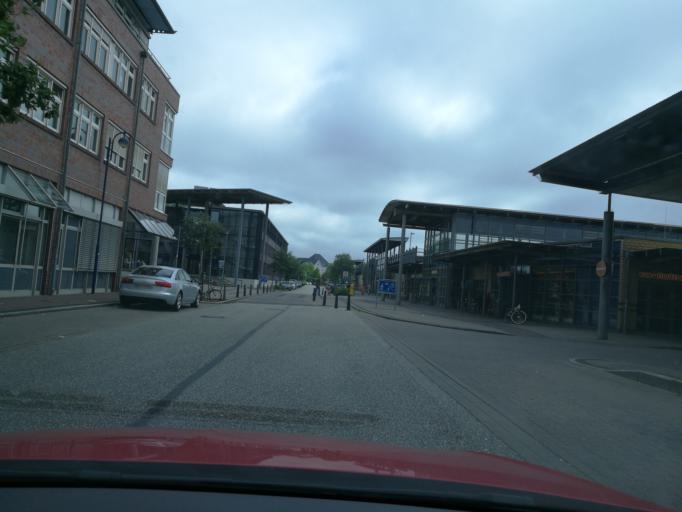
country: DE
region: Schleswig-Holstein
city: Bad Oldesloe
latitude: 53.8053
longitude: 10.3813
